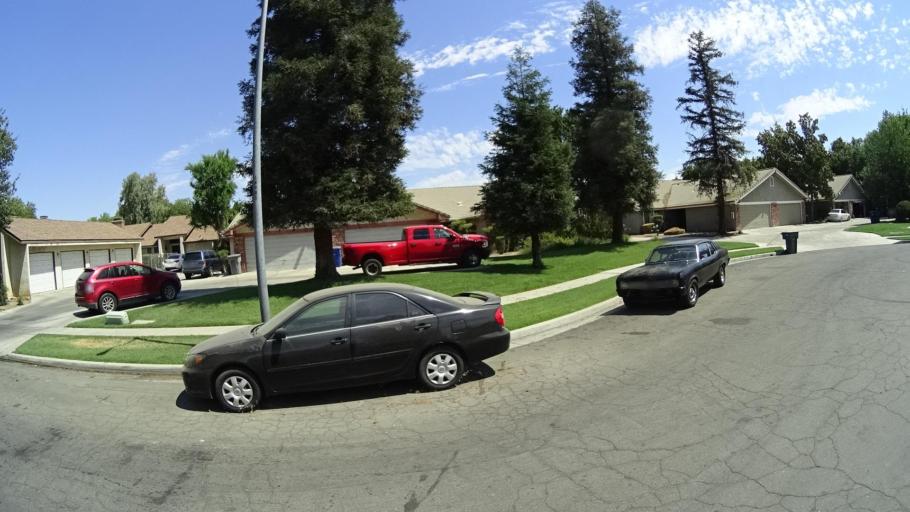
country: US
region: California
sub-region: Fresno County
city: Sunnyside
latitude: 36.7295
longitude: -119.7170
